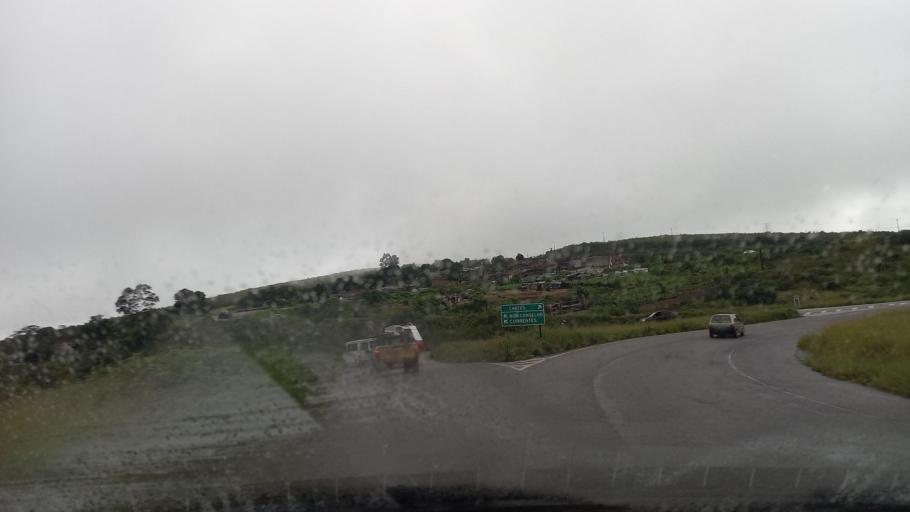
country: BR
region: Pernambuco
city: Garanhuns
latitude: -8.8782
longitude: -36.5076
